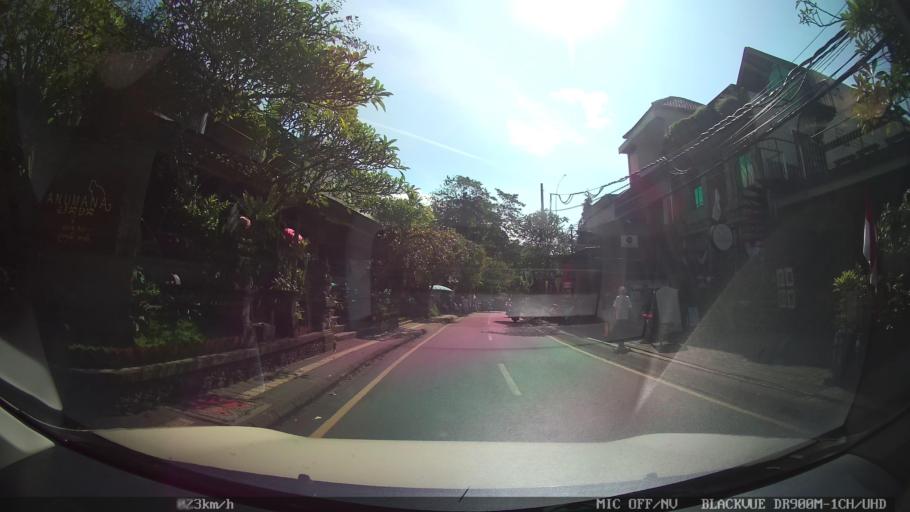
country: ID
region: Bali
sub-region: Kabupaten Gianyar
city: Ubud
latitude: -8.5183
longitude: 115.2625
